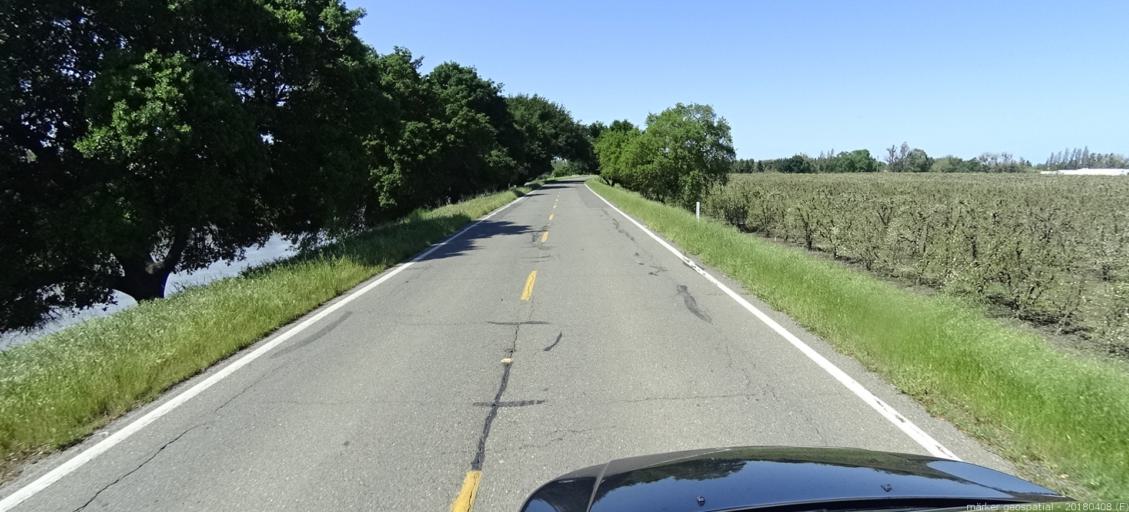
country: US
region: California
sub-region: Sacramento County
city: Walnut Grove
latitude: 38.3085
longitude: -121.5742
